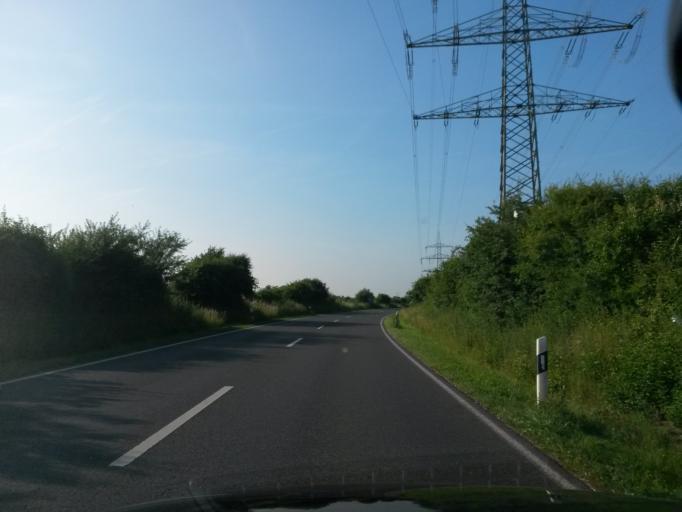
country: DE
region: North Rhine-Westphalia
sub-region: Regierungsbezirk Koln
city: Alfter
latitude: 50.7290
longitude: 7.0333
